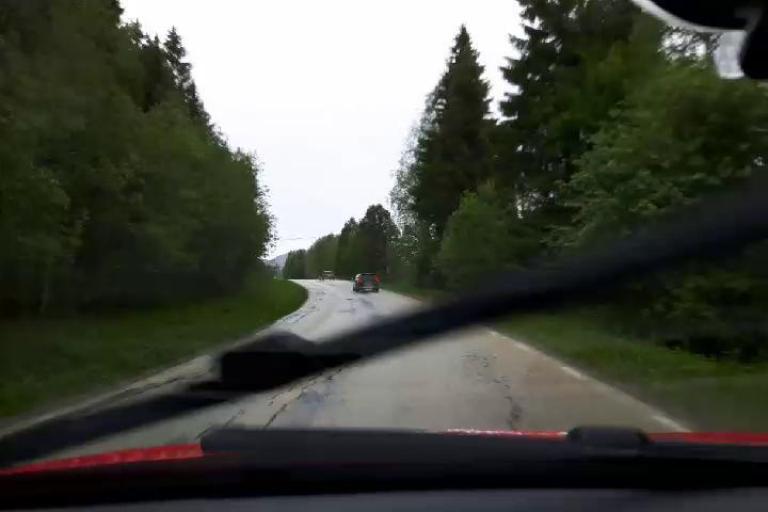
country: SE
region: Jaemtland
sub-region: Bergs Kommun
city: Hoverberg
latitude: 62.7880
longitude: 14.4371
